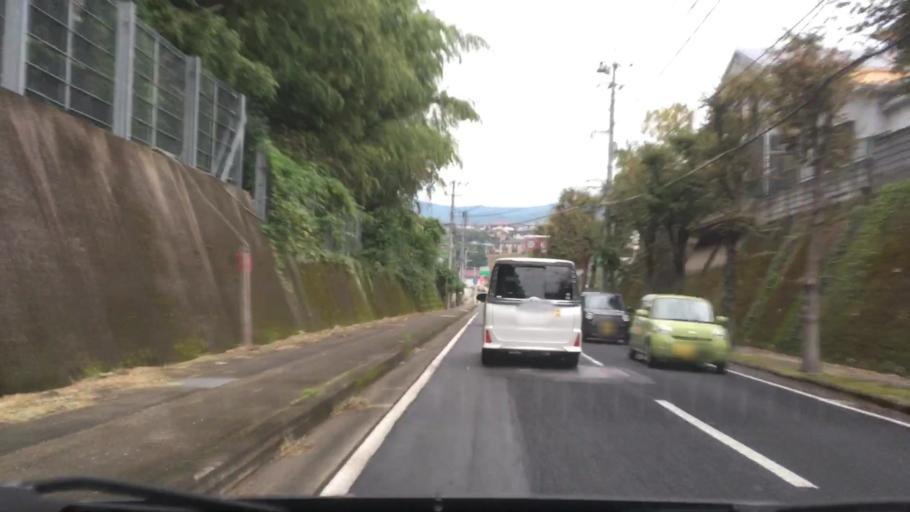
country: JP
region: Nagasaki
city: Sasebo
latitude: 33.1289
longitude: 129.7923
